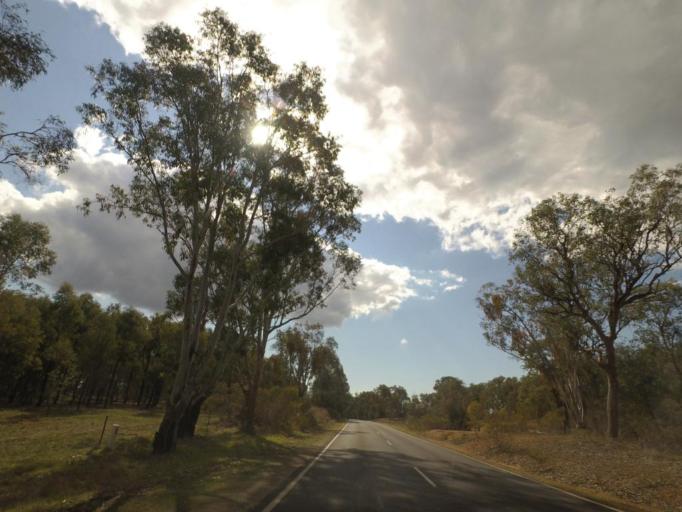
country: AU
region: New South Wales
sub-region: Corowa Shire
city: Howlong
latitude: -36.1748
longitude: 146.6077
